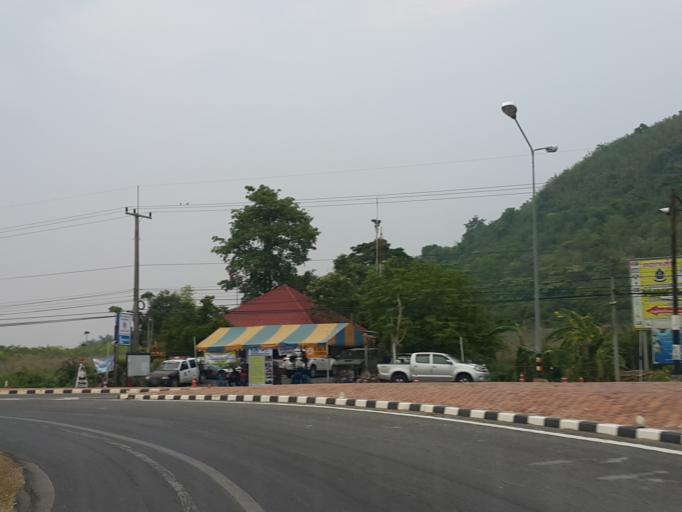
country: TH
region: Uthai Thani
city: Ban Rai
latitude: 15.0859
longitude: 99.5857
